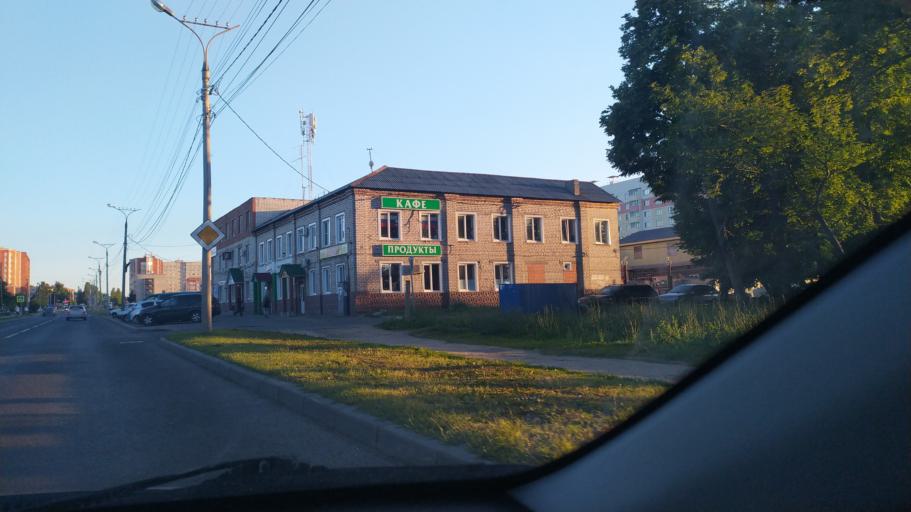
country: RU
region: Chuvashia
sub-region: Cheboksarskiy Rayon
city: Cheboksary
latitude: 56.1190
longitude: 47.2247
